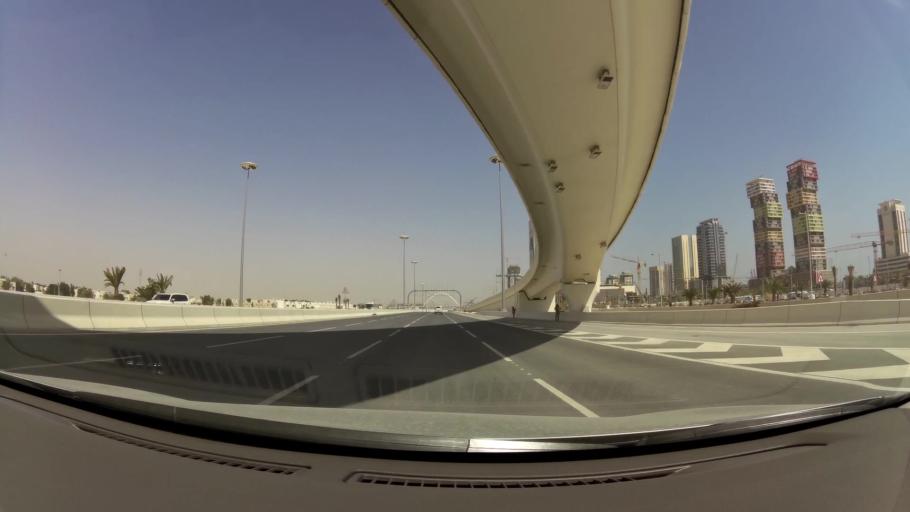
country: QA
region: Baladiyat ad Dawhah
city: Doha
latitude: 25.3827
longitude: 51.5210
